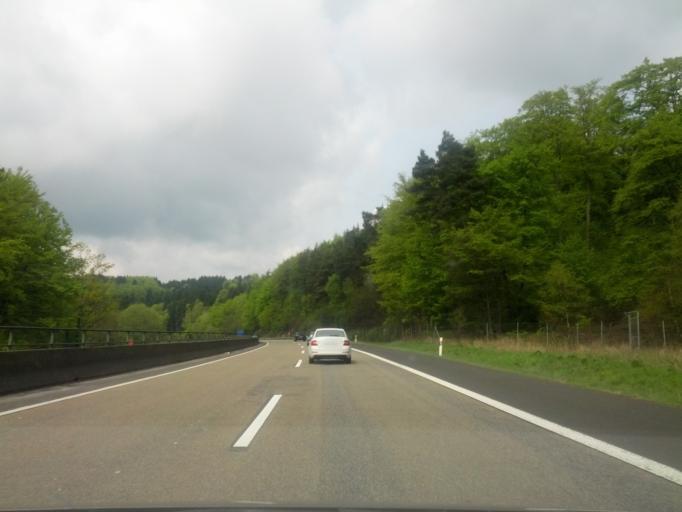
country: DE
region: Hesse
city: Grebenau
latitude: 50.7924
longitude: 9.4571
